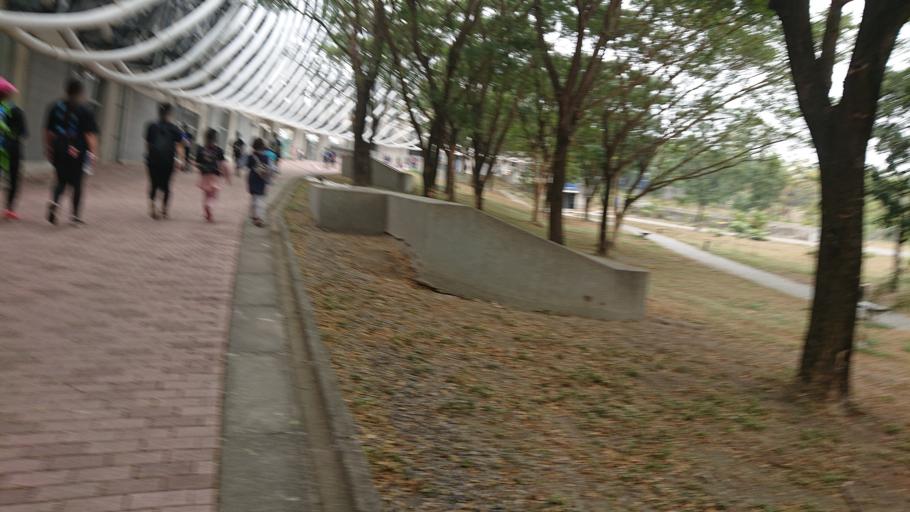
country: TW
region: Kaohsiung
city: Kaohsiung
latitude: 22.7017
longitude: 120.2961
